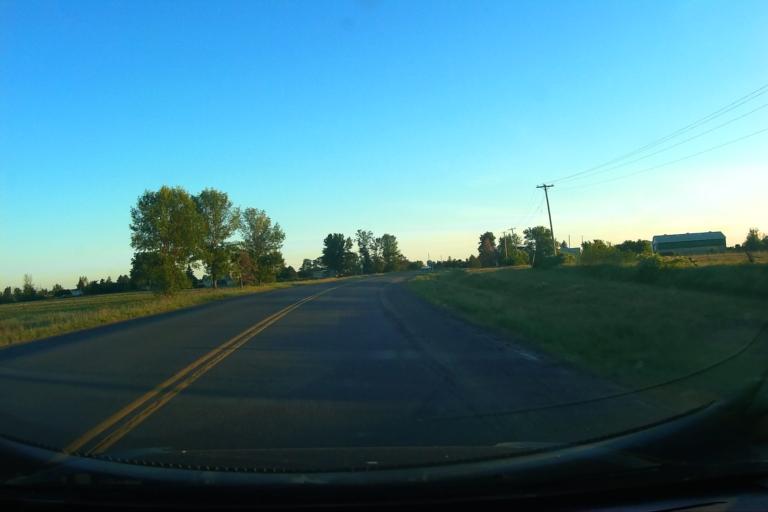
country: CA
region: Ontario
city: Casselman
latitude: 45.0797
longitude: -75.2114
